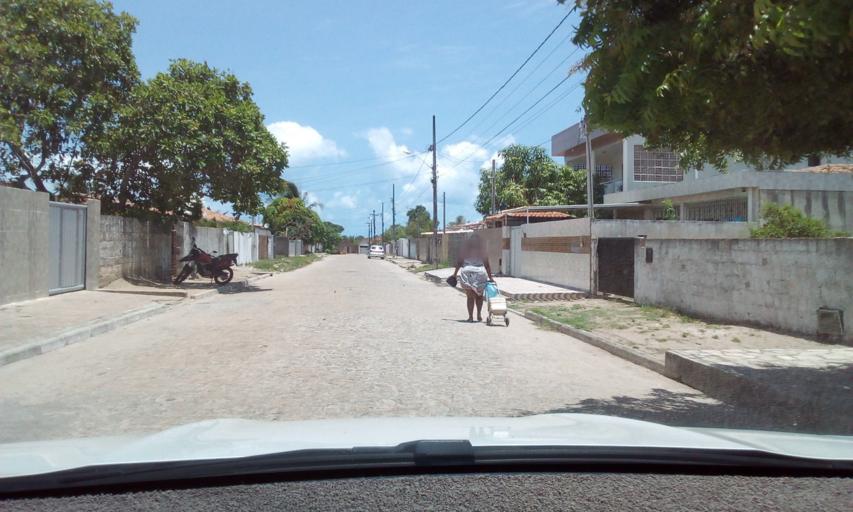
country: BR
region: Paraiba
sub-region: Joao Pessoa
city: Joao Pessoa
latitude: -7.1764
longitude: -34.8169
